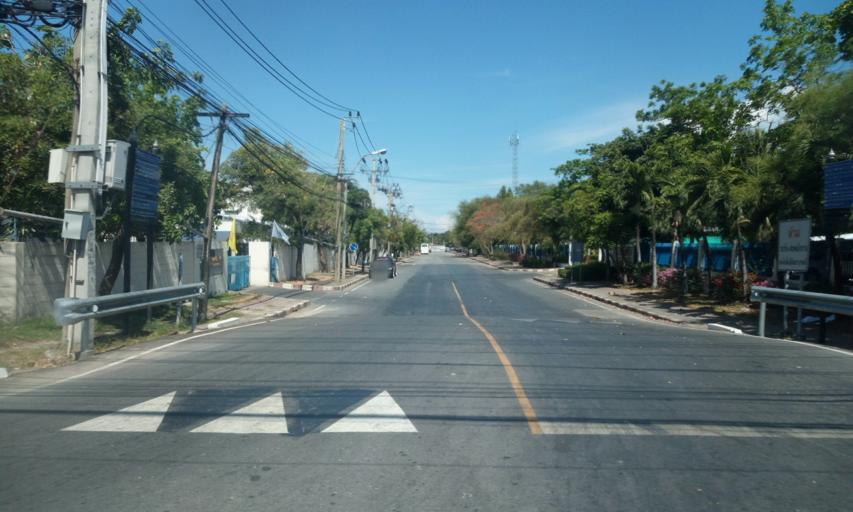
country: TH
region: Samut Prakan
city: Bang Bo District
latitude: 13.5794
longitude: 100.7957
